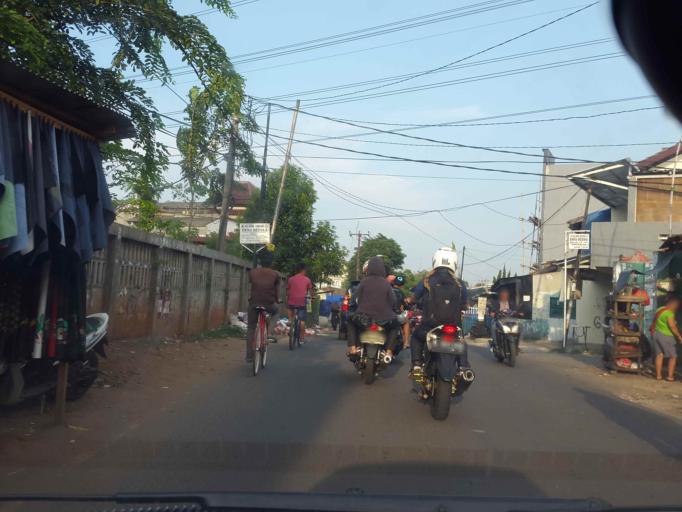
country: ID
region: Banten
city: South Tangerang
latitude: -6.2598
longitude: 106.7411
